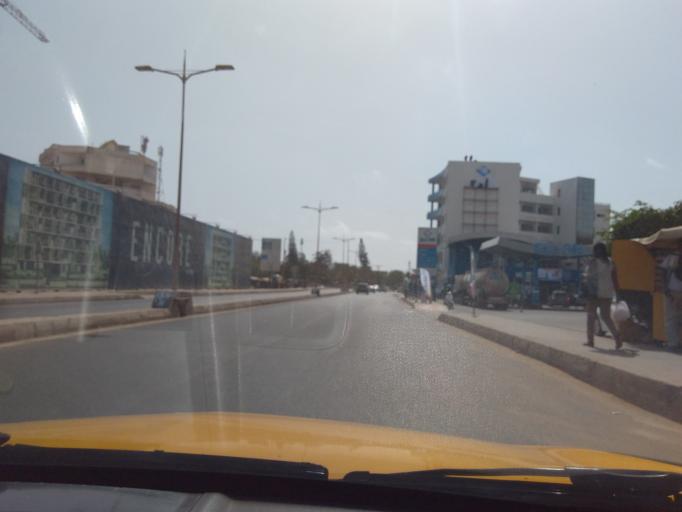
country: SN
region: Dakar
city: Mermoz Boabab
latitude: 14.7035
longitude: -17.4749
